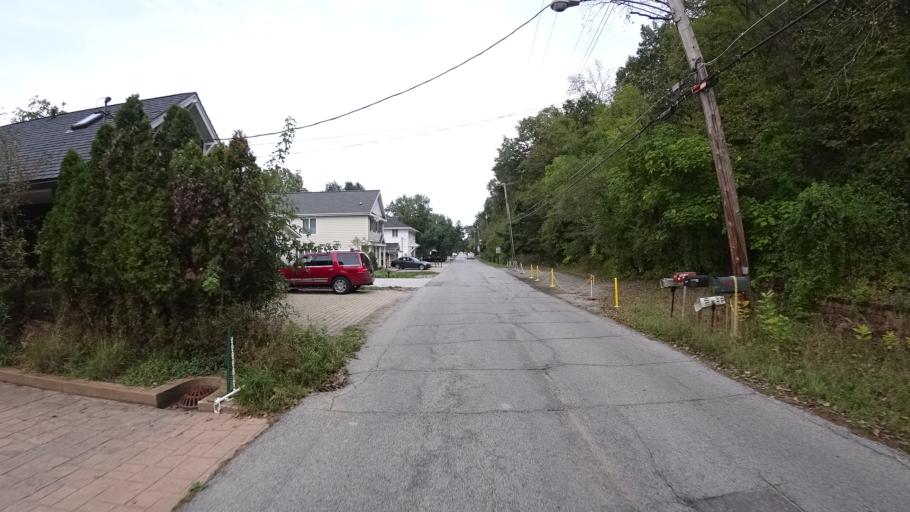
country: US
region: Indiana
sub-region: LaPorte County
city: Long Beach
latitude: 41.7377
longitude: -86.8732
